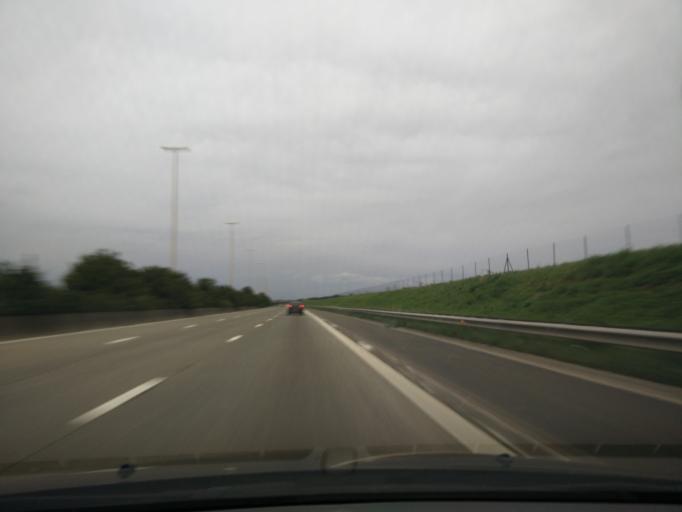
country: BE
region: Wallonia
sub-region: Province de Liege
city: Geer
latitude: 50.7012
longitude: 5.1451
